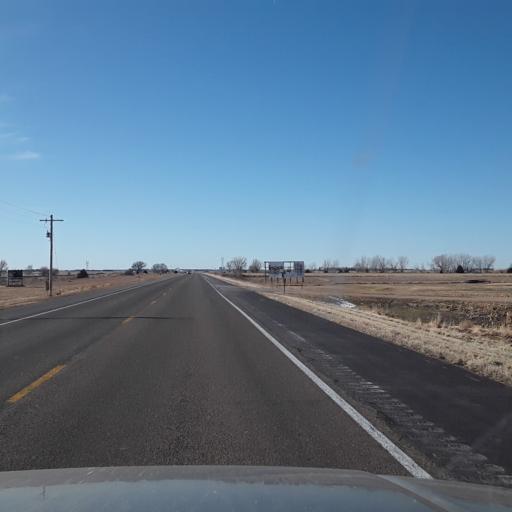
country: US
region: Nebraska
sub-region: Kearney County
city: Minden
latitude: 40.5377
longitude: -98.8627
